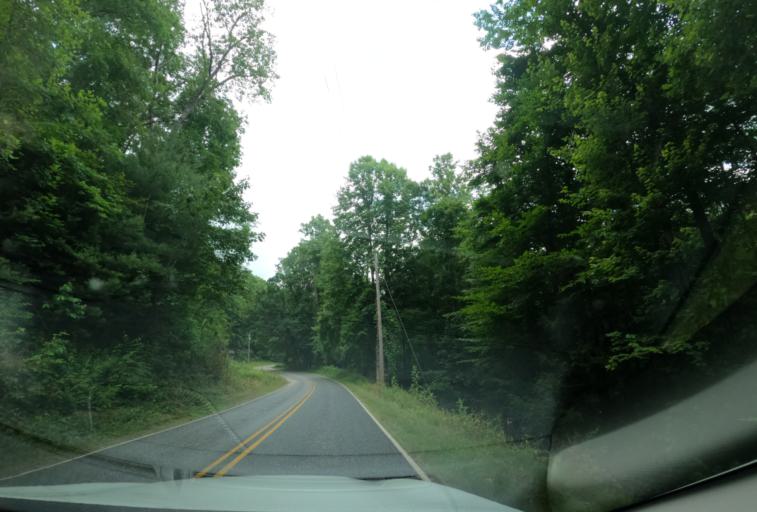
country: US
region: North Carolina
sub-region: Haywood County
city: Hazelwood
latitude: 35.3951
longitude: -82.8962
